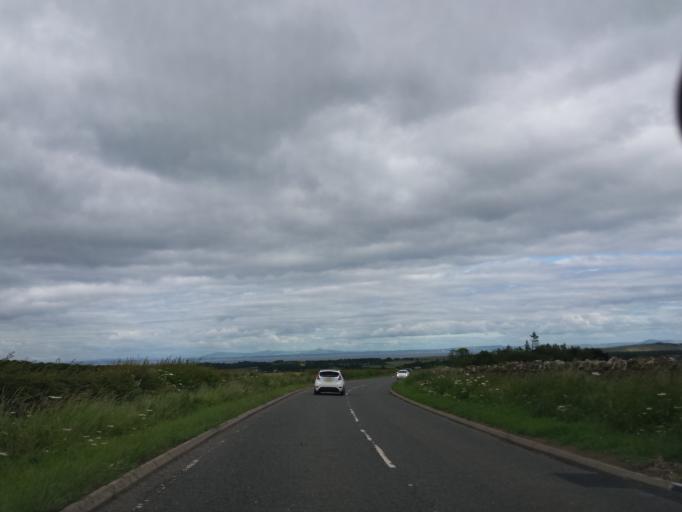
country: GB
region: Scotland
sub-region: East Lothian
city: Haddington
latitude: 55.9832
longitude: -2.8238
